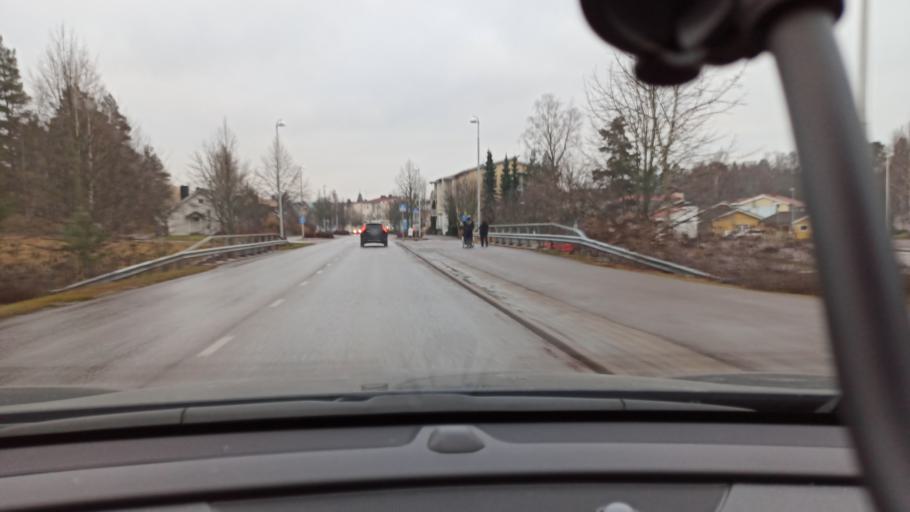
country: FI
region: Uusimaa
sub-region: Helsinki
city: Kirkkonummi
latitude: 60.1292
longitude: 24.4343
